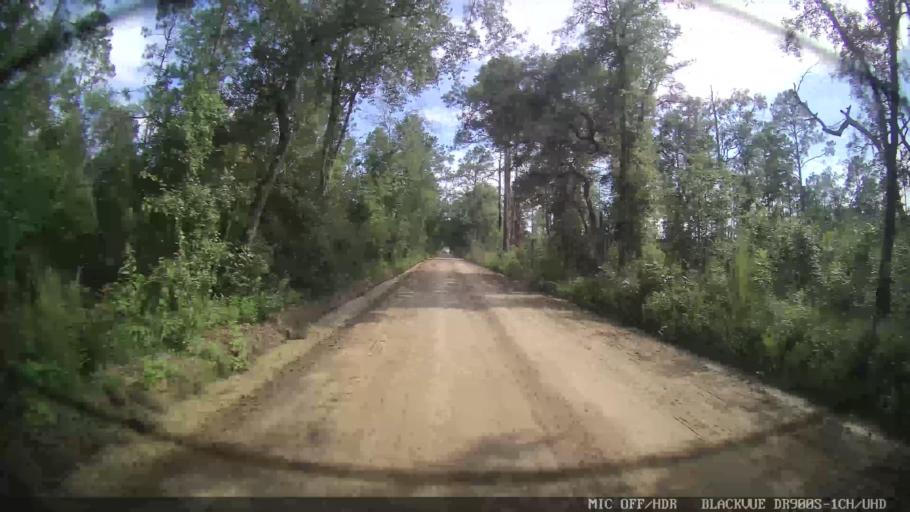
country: US
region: Georgia
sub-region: Echols County
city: Statenville
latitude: 30.6225
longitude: -83.2001
